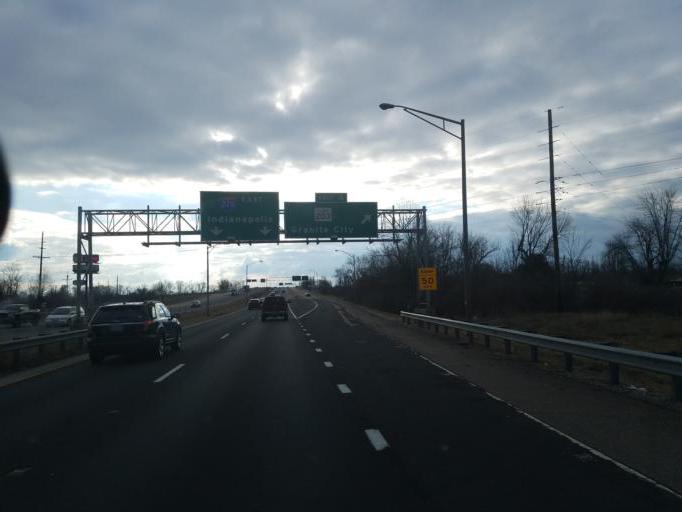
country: US
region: Illinois
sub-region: Madison County
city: Mitchell
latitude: 38.7622
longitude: -90.1019
